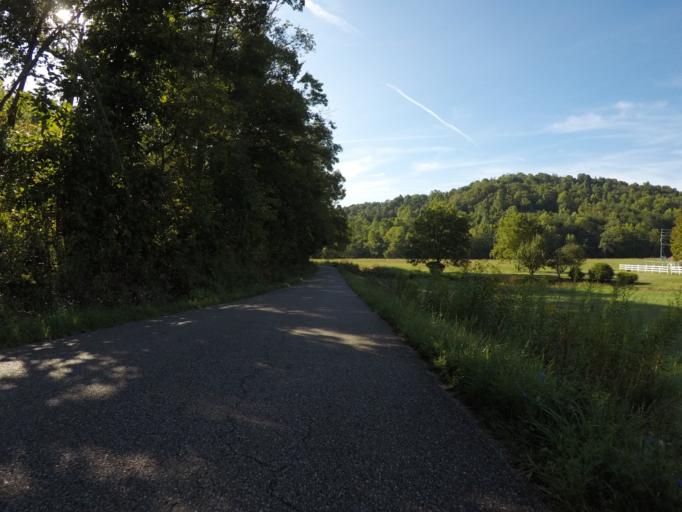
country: US
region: Ohio
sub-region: Lawrence County
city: Burlington
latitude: 38.5004
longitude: -82.5119
